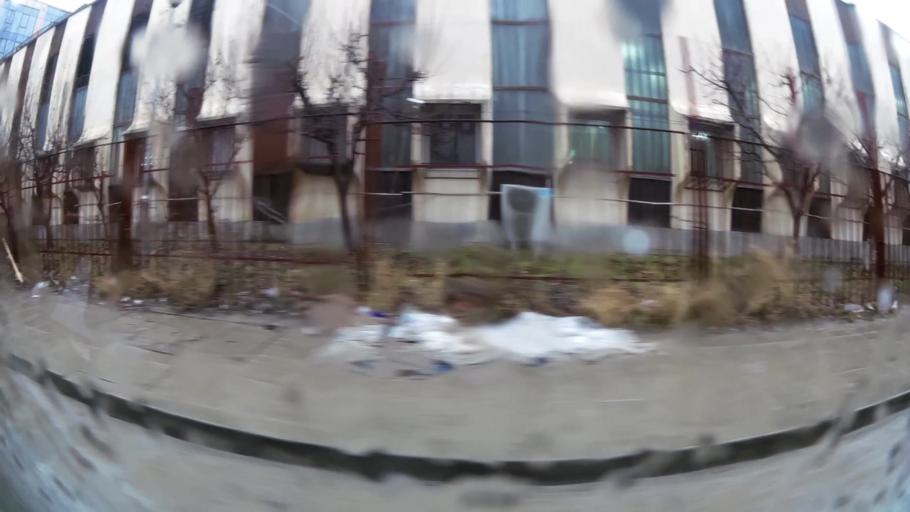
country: BG
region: Sofia-Capital
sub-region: Stolichna Obshtina
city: Sofia
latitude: 42.6626
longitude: 23.3815
